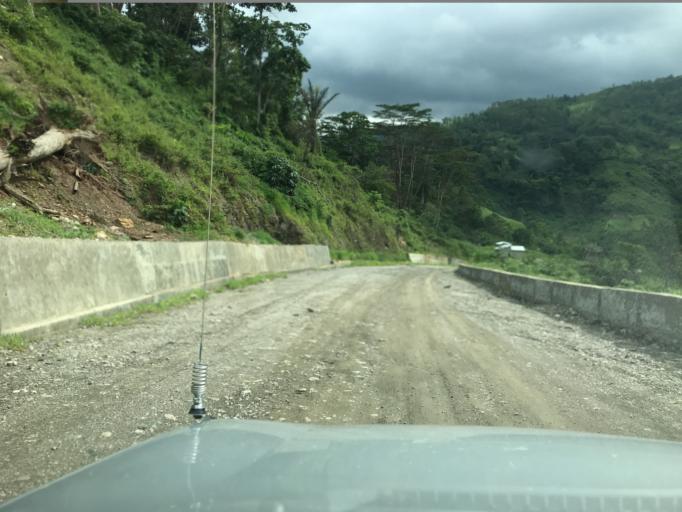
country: TL
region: Aileu
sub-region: Aileu Villa
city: Aileu
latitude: -8.6470
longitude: 125.5263
